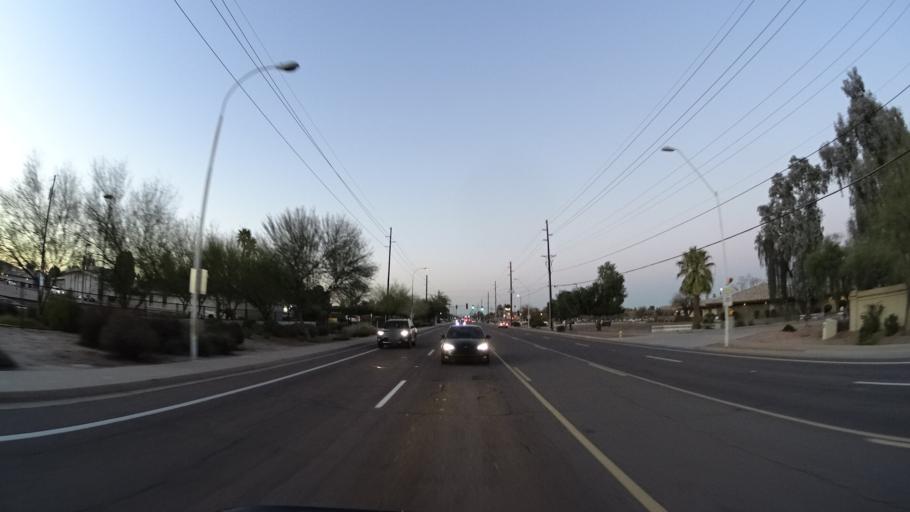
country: US
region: Arizona
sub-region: Maricopa County
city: San Carlos
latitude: 33.3229
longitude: -111.8765
